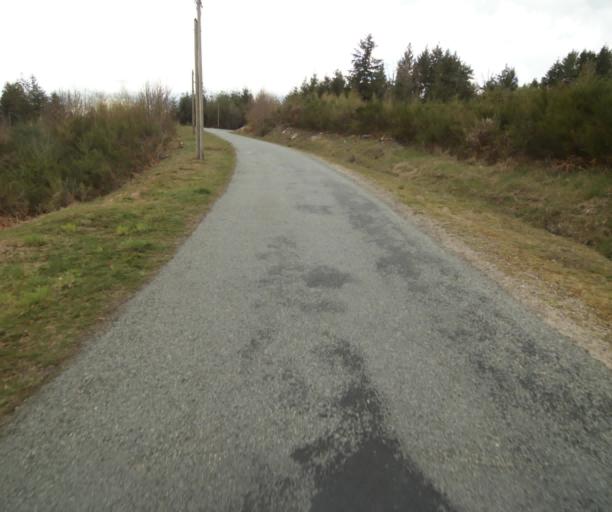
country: FR
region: Limousin
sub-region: Departement de la Correze
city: Correze
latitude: 45.3207
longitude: 1.9353
